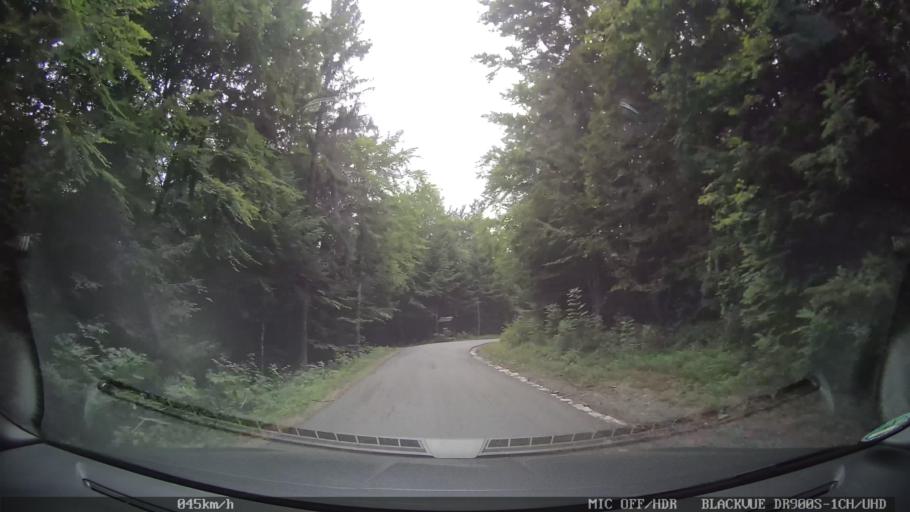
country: HR
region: Licko-Senjska
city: Jezerce
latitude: 44.9261
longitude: 15.5707
